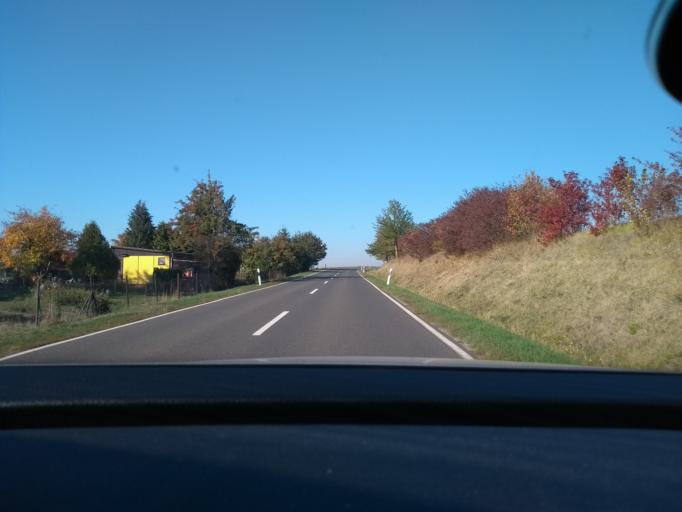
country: DE
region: Saxony-Anhalt
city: Farnstadt
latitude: 51.4515
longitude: 11.5837
